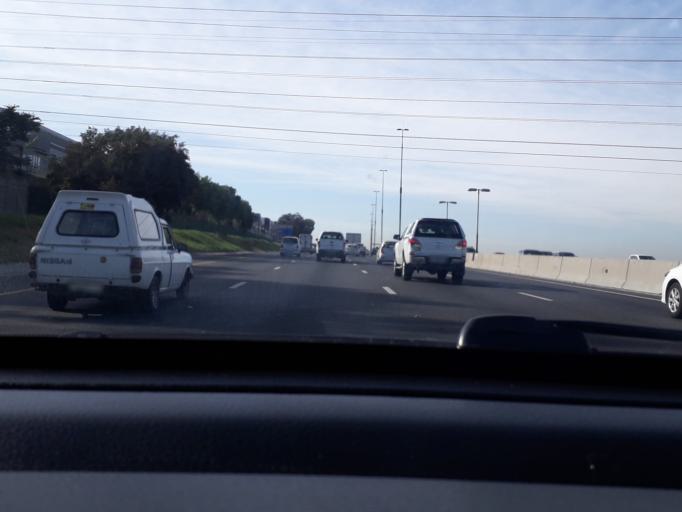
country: ZA
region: Gauteng
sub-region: City of Johannesburg Metropolitan Municipality
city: Modderfontein
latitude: -26.0622
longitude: 28.1078
